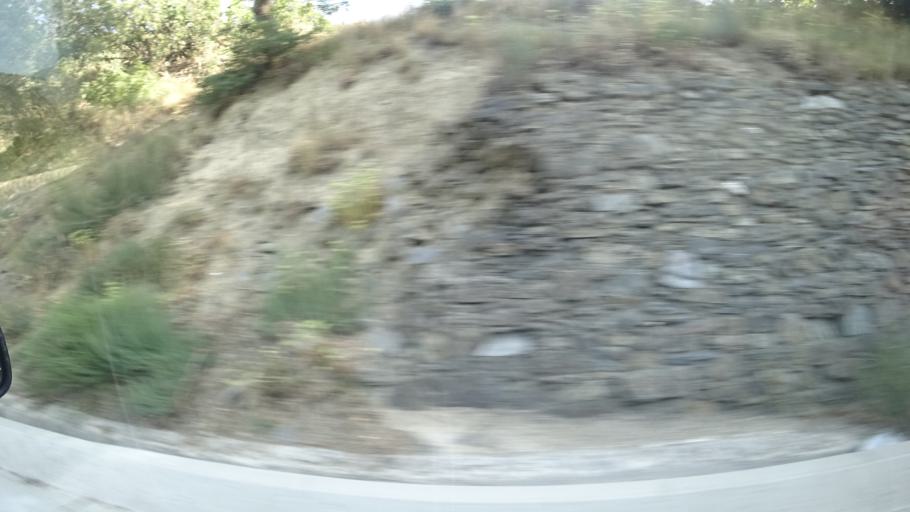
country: FR
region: Languedoc-Roussillon
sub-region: Departement des Pyrenees-Orientales
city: Vernet-les-Bains
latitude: 42.5614
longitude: 2.2964
